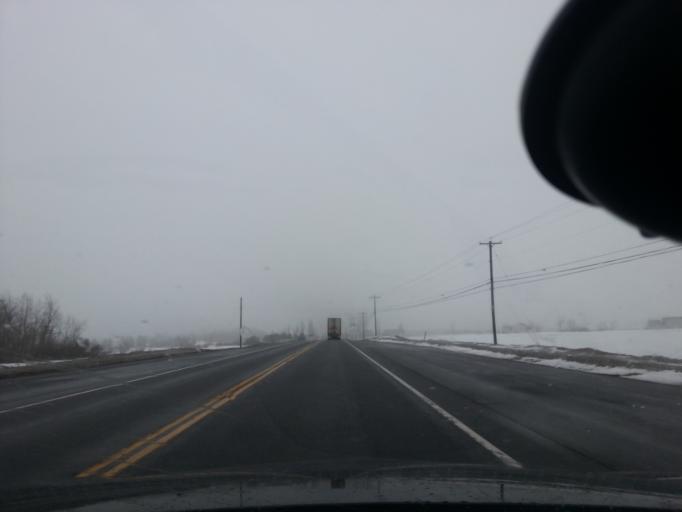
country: US
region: New York
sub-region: Jefferson County
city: Fort Drum
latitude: 44.1125
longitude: -75.7577
